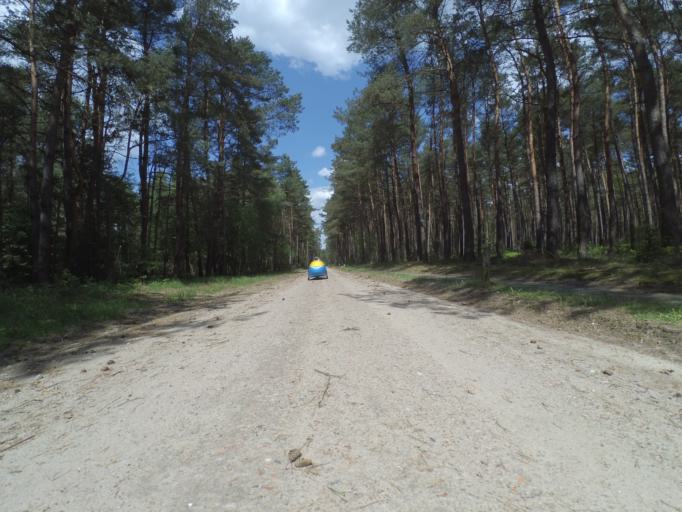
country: DE
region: Lower Saxony
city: Ummern
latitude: 52.6244
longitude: 10.4469
